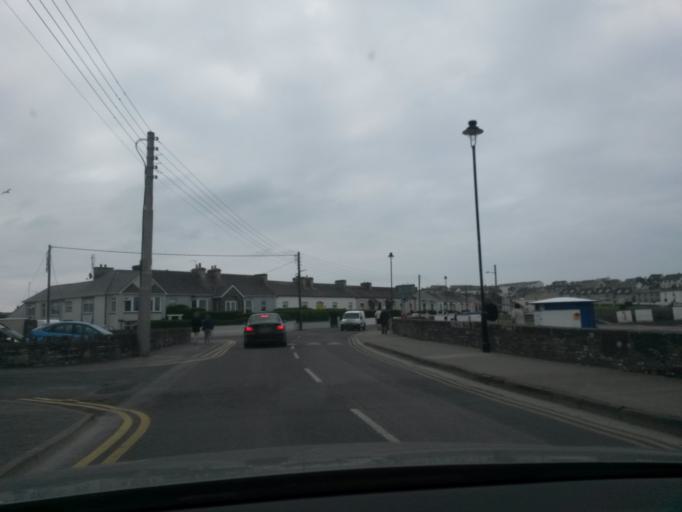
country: IE
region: Munster
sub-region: Ciarrai
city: Ballybunnion
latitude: 52.6776
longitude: -9.6522
